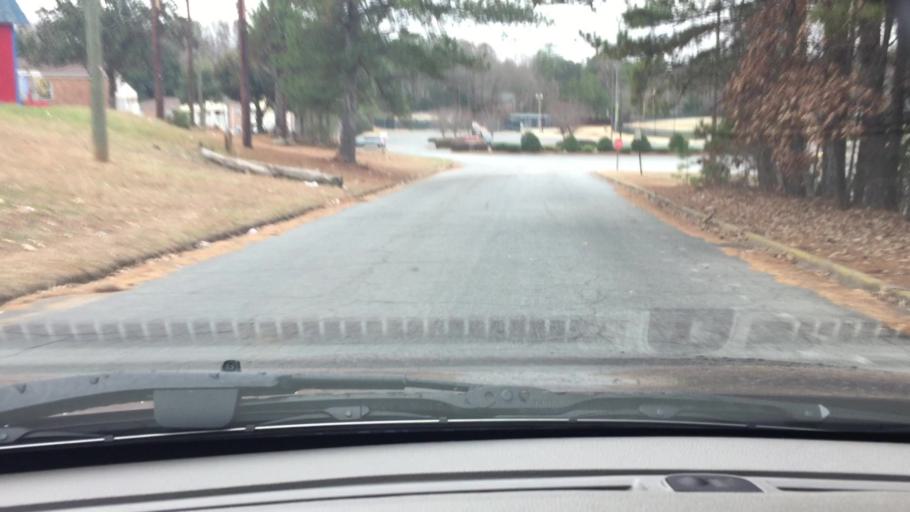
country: US
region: Georgia
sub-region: Cobb County
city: Fair Oaks
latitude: 33.8976
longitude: -84.5419
